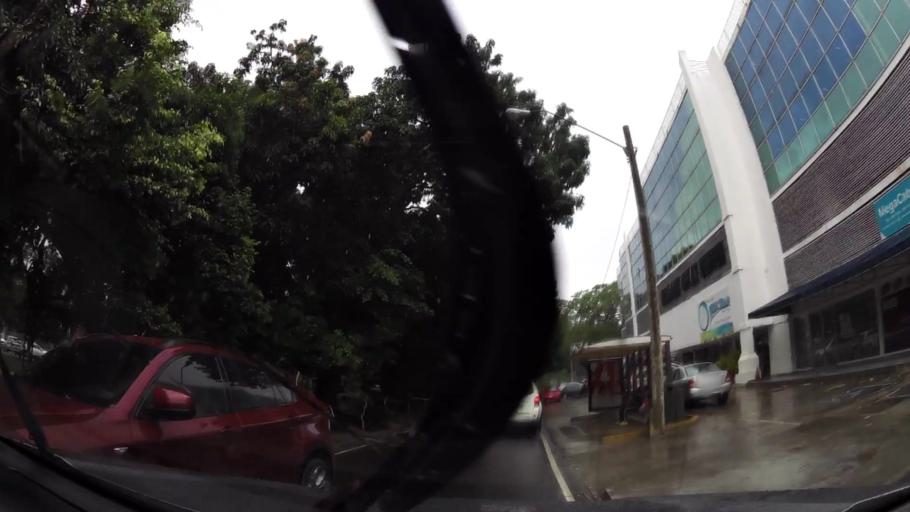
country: PA
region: Panama
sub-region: Distrito de Panama
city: Ancon
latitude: 8.9739
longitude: -79.5615
